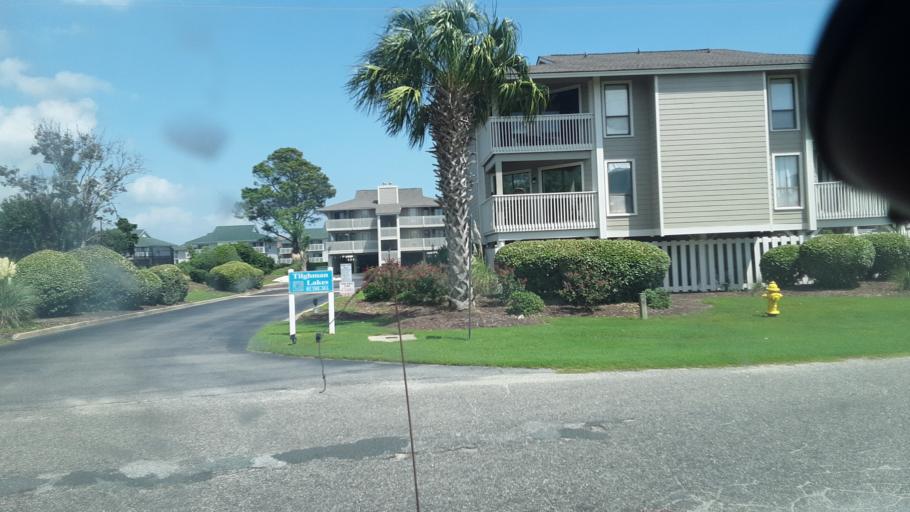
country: US
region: South Carolina
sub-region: Horry County
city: North Myrtle Beach
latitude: 33.8276
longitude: -78.6523
